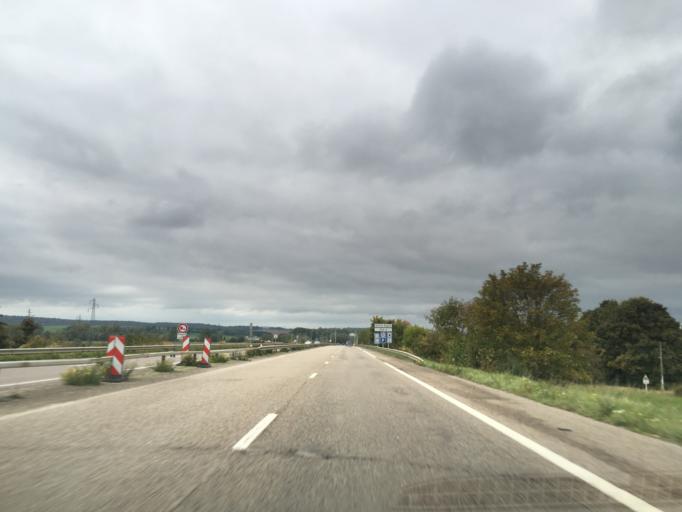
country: FR
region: Lorraine
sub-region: Departement de Meurthe-et-Moselle
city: Foug
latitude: 48.6833
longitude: 5.7344
